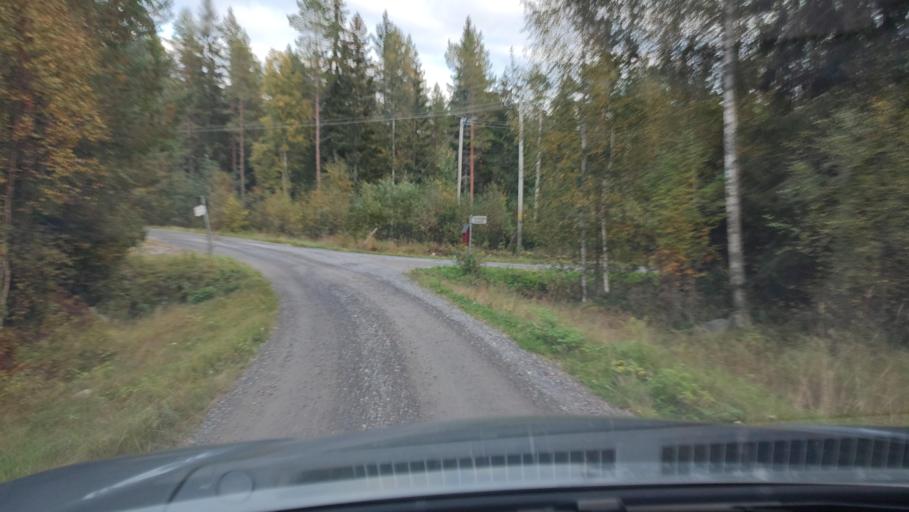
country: FI
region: Ostrobothnia
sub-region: Sydosterbotten
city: Kristinestad
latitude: 62.2302
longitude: 21.4210
